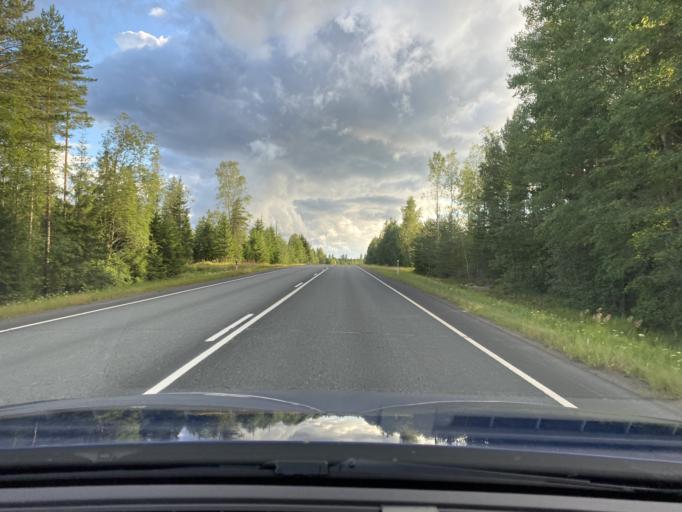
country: FI
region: Haeme
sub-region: Haemeenlinna
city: Renko
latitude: 60.8539
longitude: 24.1612
